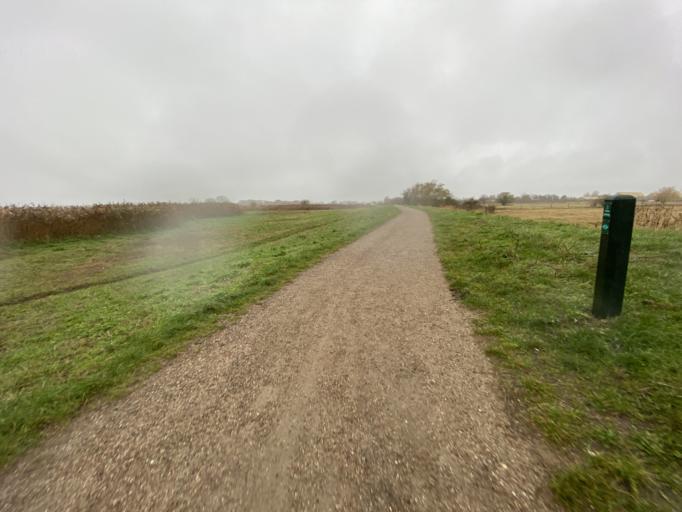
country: DK
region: Capital Region
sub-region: Dragor Kommune
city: Dragor
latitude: 55.5777
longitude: 12.6403
